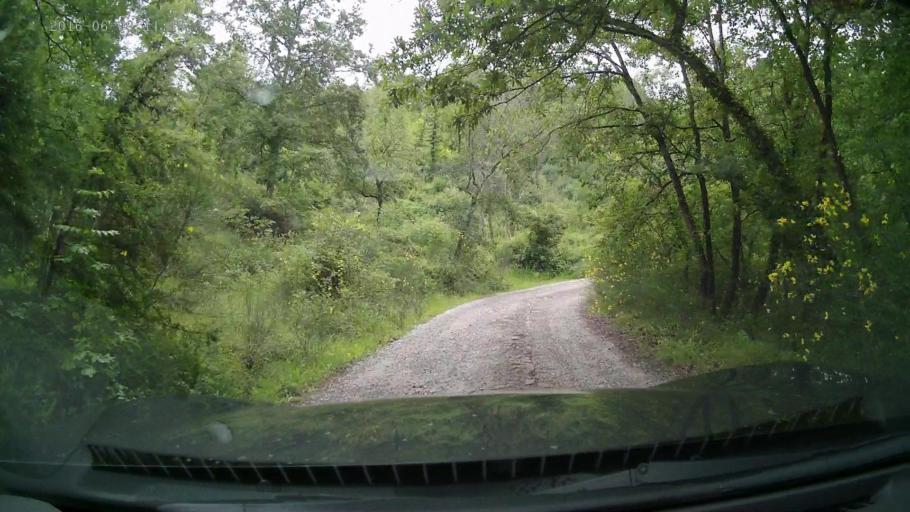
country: IT
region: Tuscany
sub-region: Province of Florence
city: Greve in Chianti
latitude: 43.5678
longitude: 11.2991
